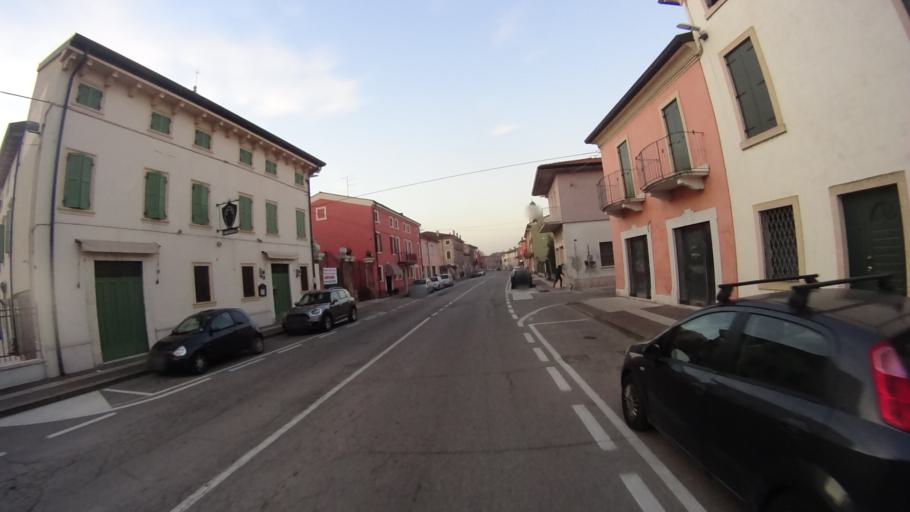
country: IT
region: Veneto
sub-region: Provincia di Verona
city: Povegliano Veronese
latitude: 45.3447
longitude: 10.8822
